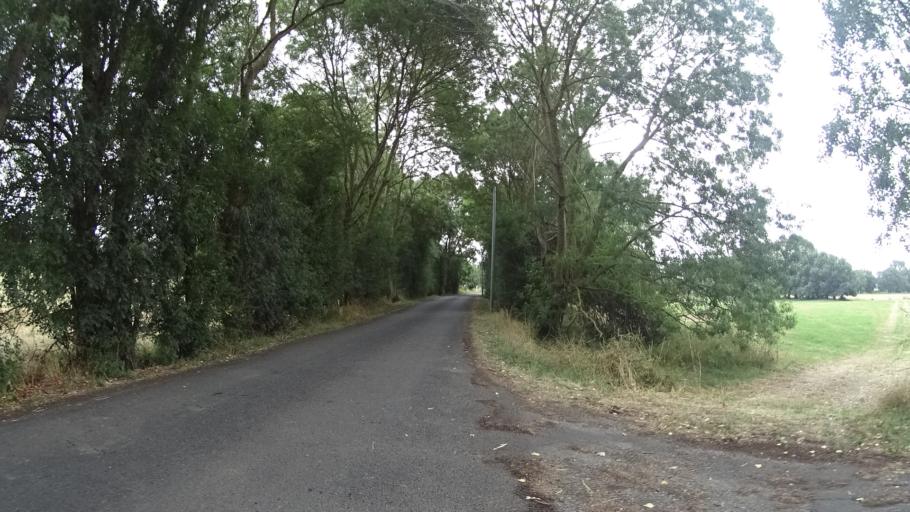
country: FR
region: Pays de la Loire
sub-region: Departement de Maine-et-Loire
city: Montjean-sur-Loire
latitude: 47.3892
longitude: -0.8448
